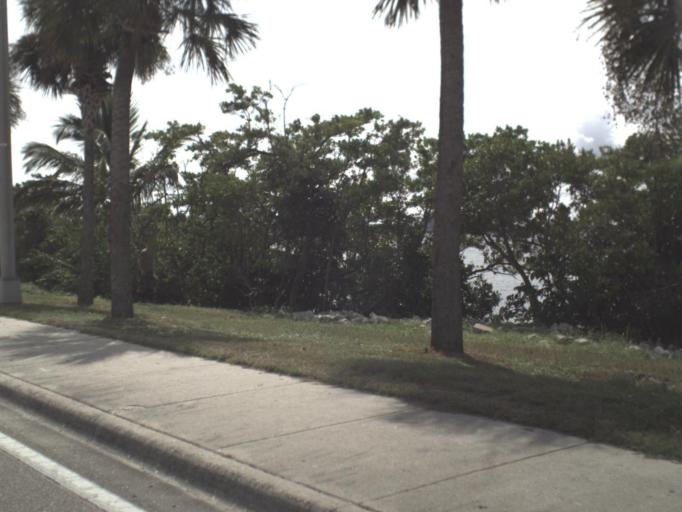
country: US
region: Florida
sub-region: Lee County
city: North Fort Myers
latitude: 26.6615
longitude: -81.8764
